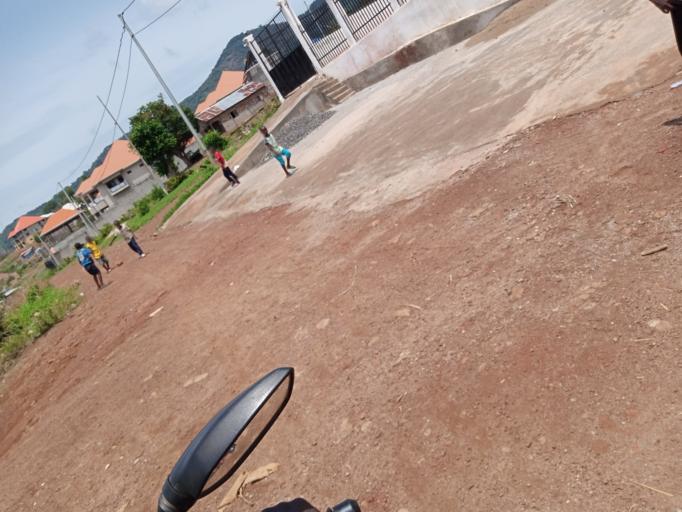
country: SL
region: Western Area
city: Hastings
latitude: 8.3725
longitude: -13.1348
